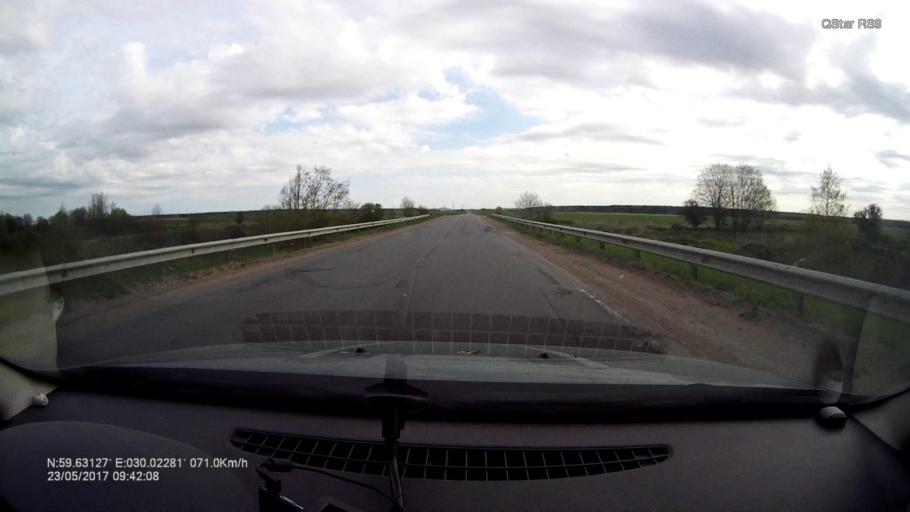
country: RU
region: Leningrad
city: Mariyenburg
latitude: 59.6316
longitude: 30.0239
